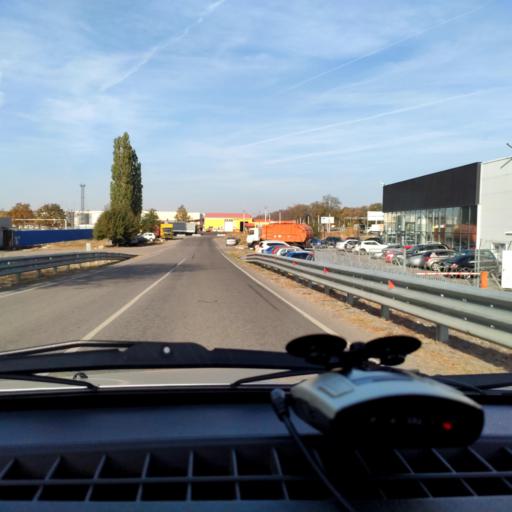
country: RU
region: Voronezj
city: Podgornoye
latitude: 51.8003
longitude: 39.2012
